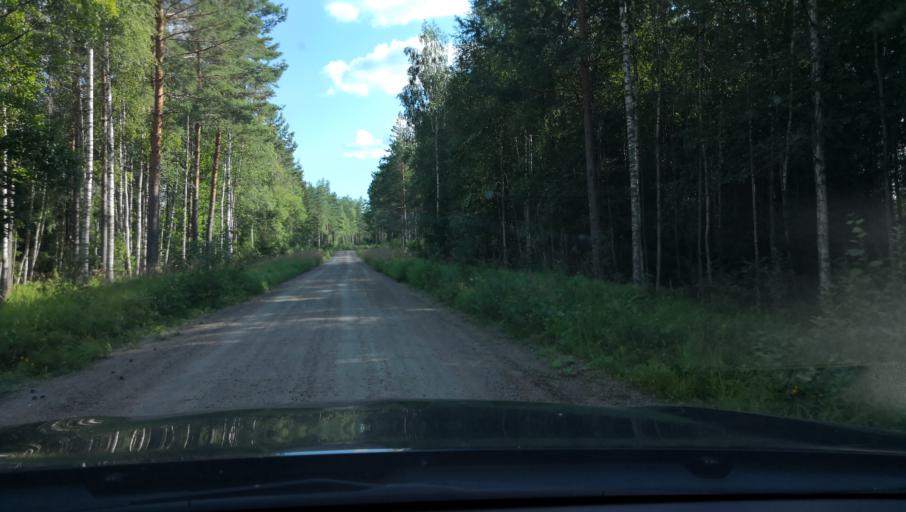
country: SE
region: Vaestmanland
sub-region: Vasteras
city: Skultuna
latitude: 59.7192
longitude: 16.3724
